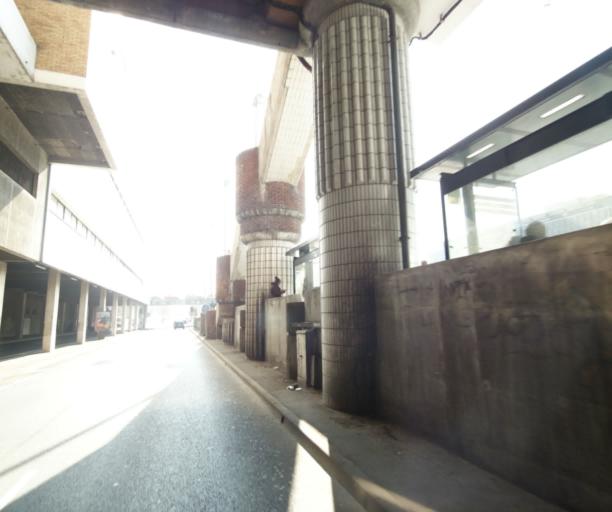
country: FR
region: Ile-de-France
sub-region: Departement du Val-d'Oise
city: Cergy-Pontoise
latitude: 49.0366
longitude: 2.0803
